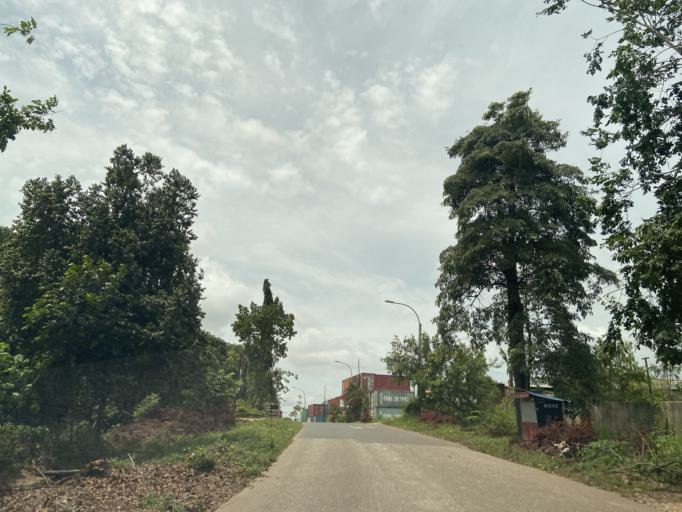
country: SG
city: Singapore
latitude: 1.1606
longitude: 104.0044
